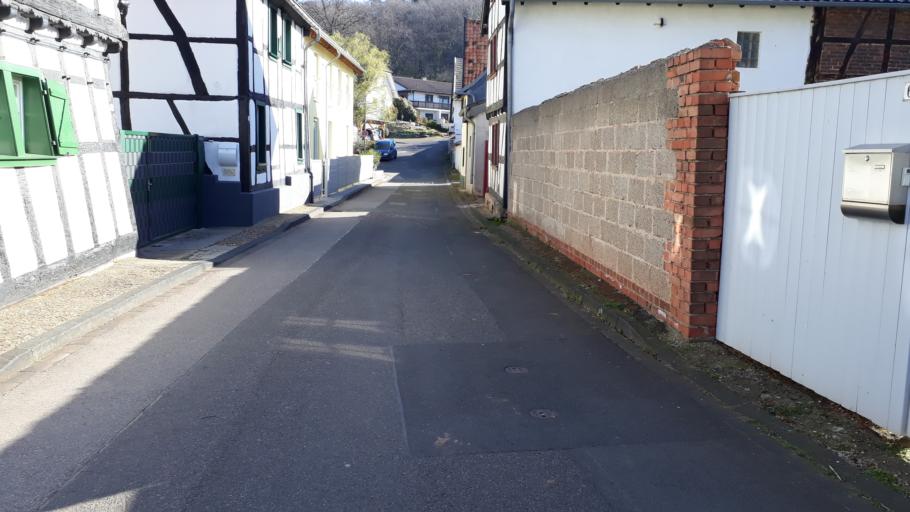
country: DE
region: North Rhine-Westphalia
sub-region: Regierungsbezirk Koln
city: Mechernich
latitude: 50.6195
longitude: 6.6666
